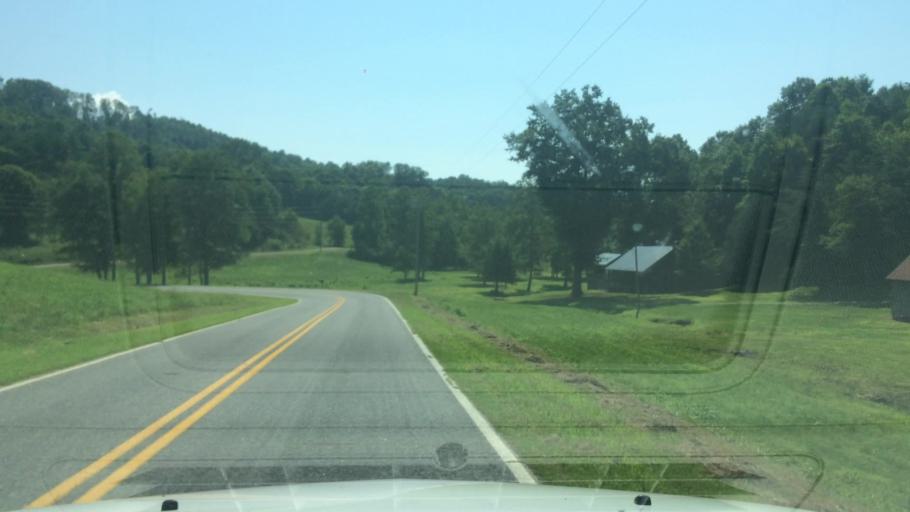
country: US
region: North Carolina
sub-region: Alexander County
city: Taylorsville
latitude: 35.9943
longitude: -81.2713
